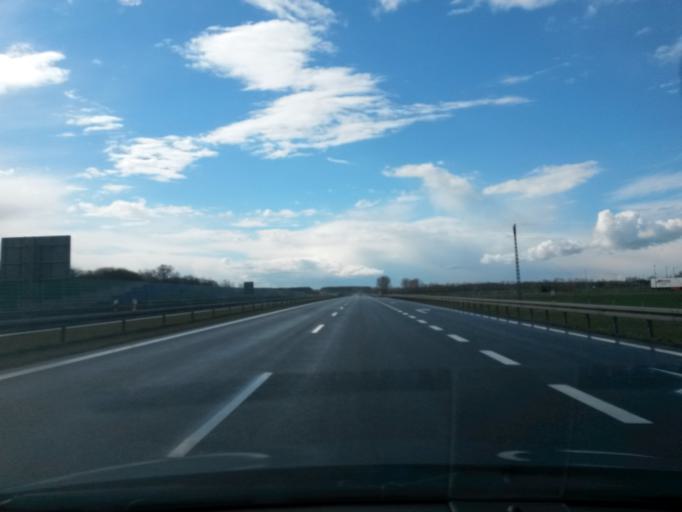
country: PL
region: Greater Poland Voivodeship
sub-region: Powiat slupecki
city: Strzalkowo
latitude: 52.2597
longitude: 17.7904
